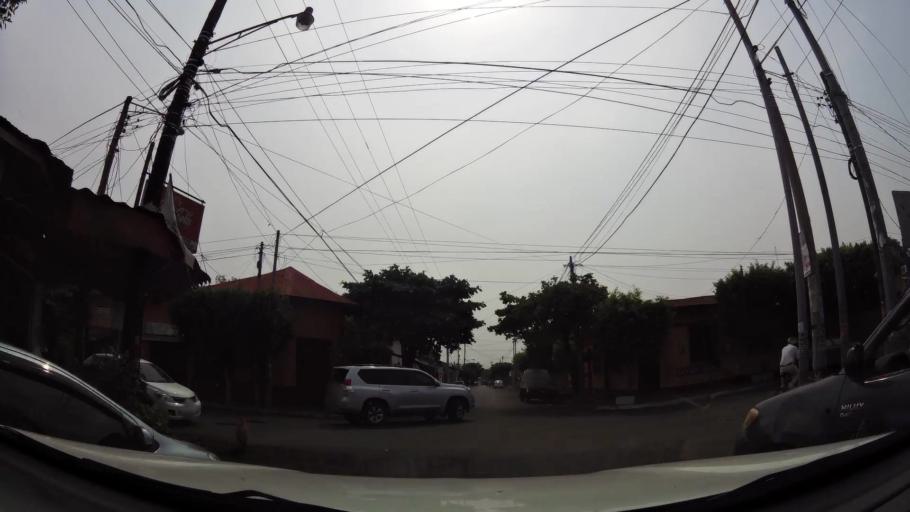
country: NI
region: Chinandega
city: Chinandega
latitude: 12.6298
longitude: -87.1342
